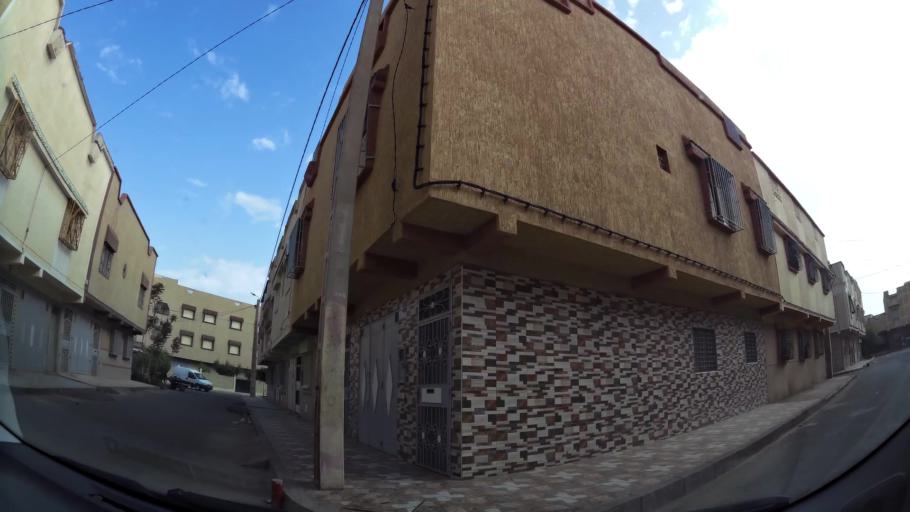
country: MA
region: Oriental
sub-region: Oujda-Angad
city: Oujda
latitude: 34.6926
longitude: -1.9015
